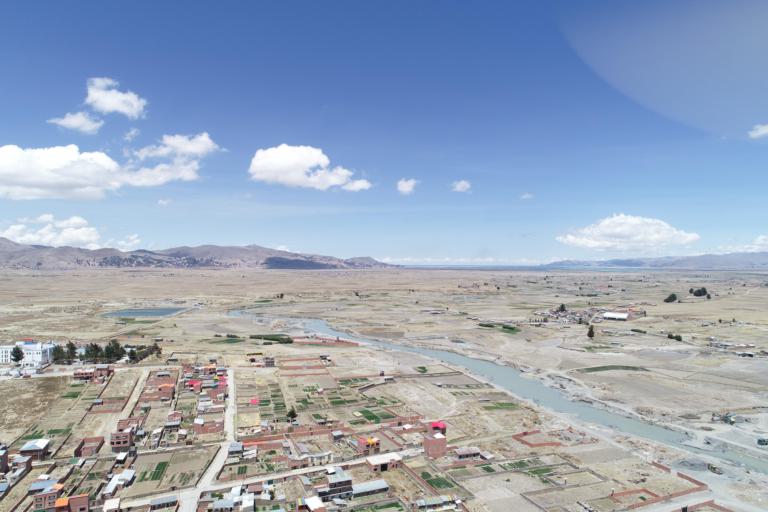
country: BO
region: La Paz
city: Achacachi
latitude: -16.0410
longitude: -68.6875
